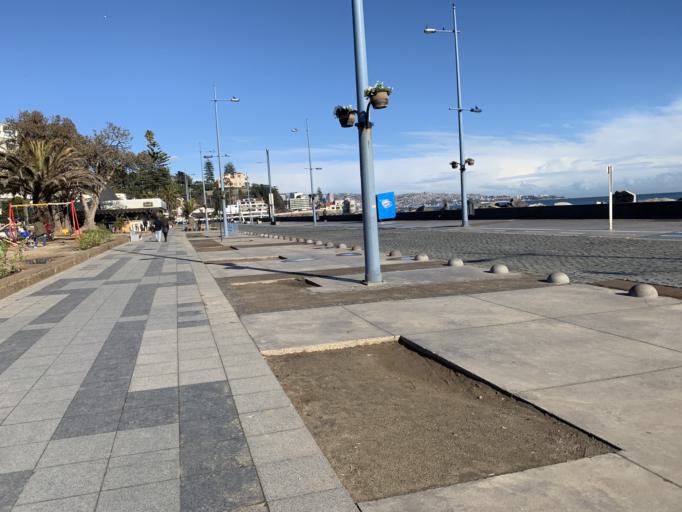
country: CL
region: Valparaiso
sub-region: Provincia de Valparaiso
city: Vina del Mar
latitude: -33.0173
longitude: -71.5597
